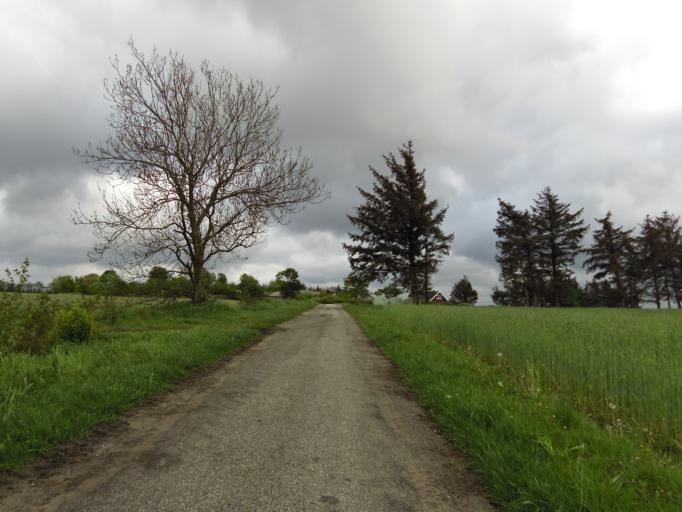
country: DK
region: South Denmark
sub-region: Haderslev Kommune
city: Gram
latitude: 55.2860
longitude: 8.9437
